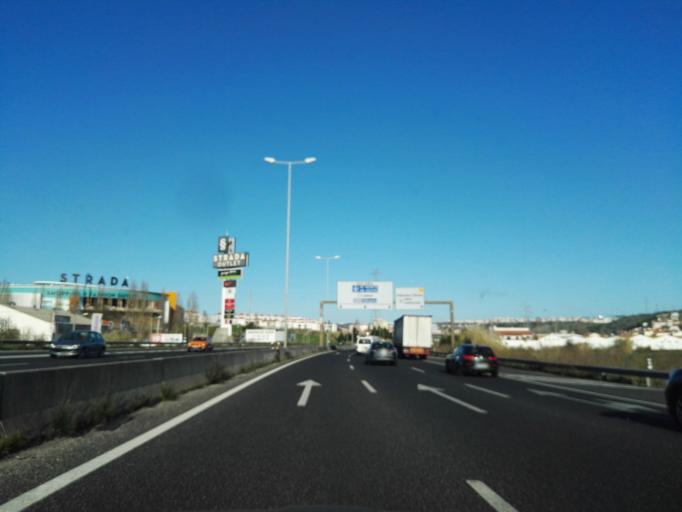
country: PT
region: Lisbon
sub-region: Odivelas
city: Pontinha
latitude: 38.7793
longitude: -9.1935
